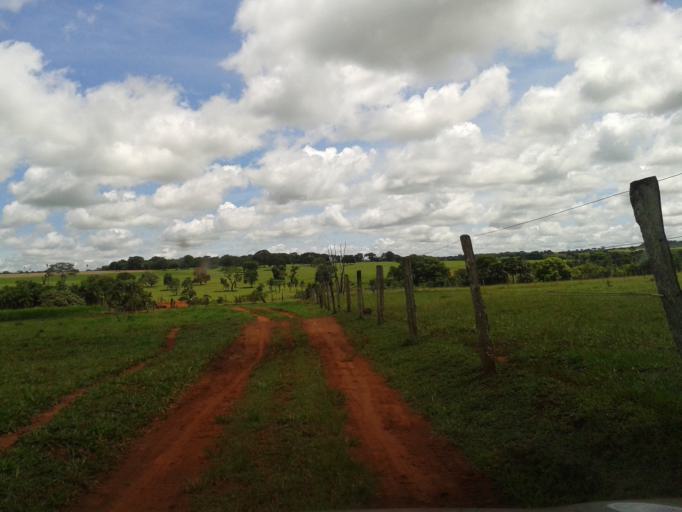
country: BR
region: Minas Gerais
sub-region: Santa Vitoria
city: Santa Vitoria
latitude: -18.7898
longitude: -49.8560
